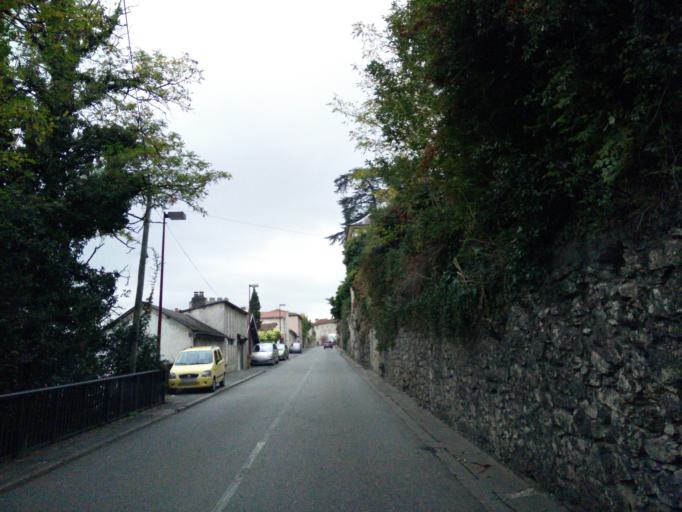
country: FR
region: Midi-Pyrenees
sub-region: Departement du Lot
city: Cahors
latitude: 44.4566
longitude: 1.4384
